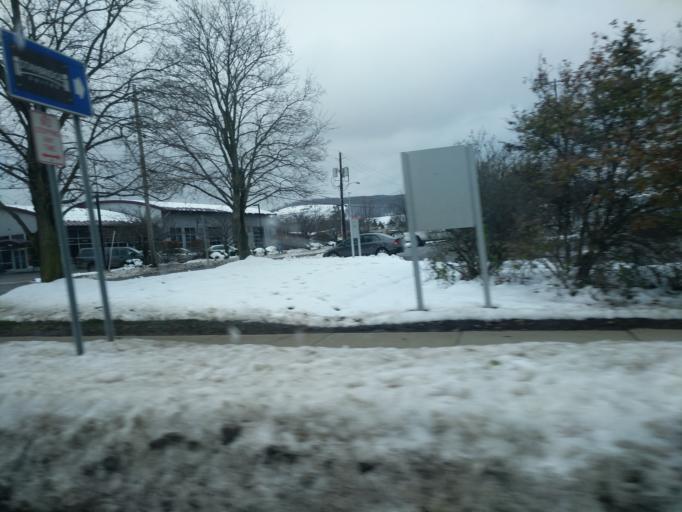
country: US
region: New York
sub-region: Steuben County
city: Corning
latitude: 42.1515
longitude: -77.0543
